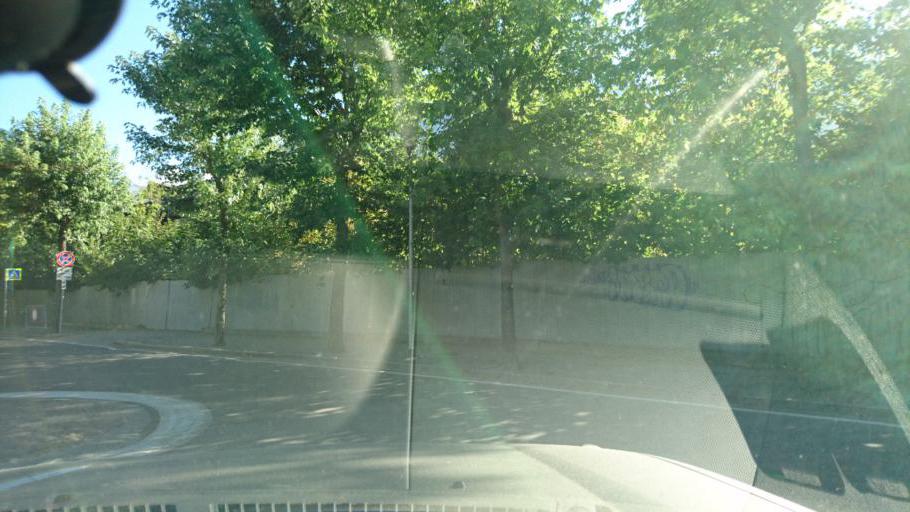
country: IT
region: Aosta Valley
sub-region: Valle d'Aosta
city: Courmayeur
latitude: 45.7952
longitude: 6.9696
